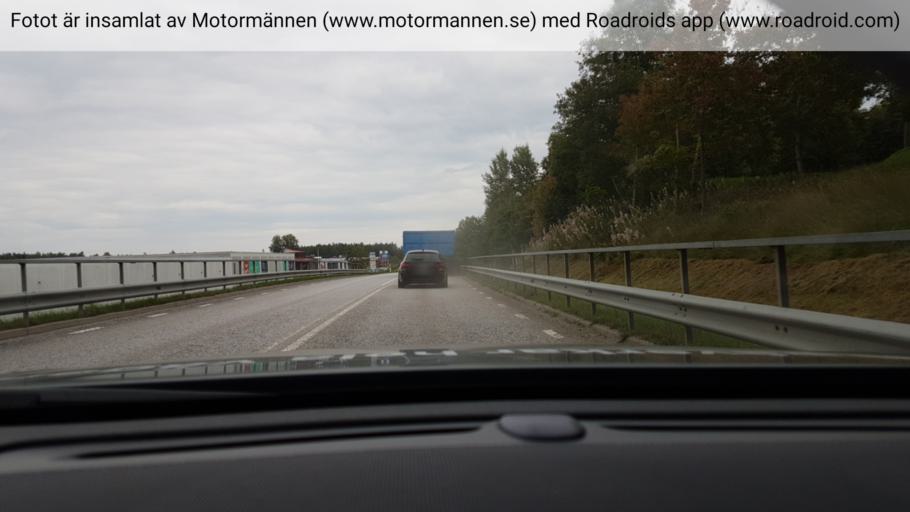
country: SE
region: Joenkoeping
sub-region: Varnamo Kommun
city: Bredaryd
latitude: 57.1716
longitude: 13.7458
